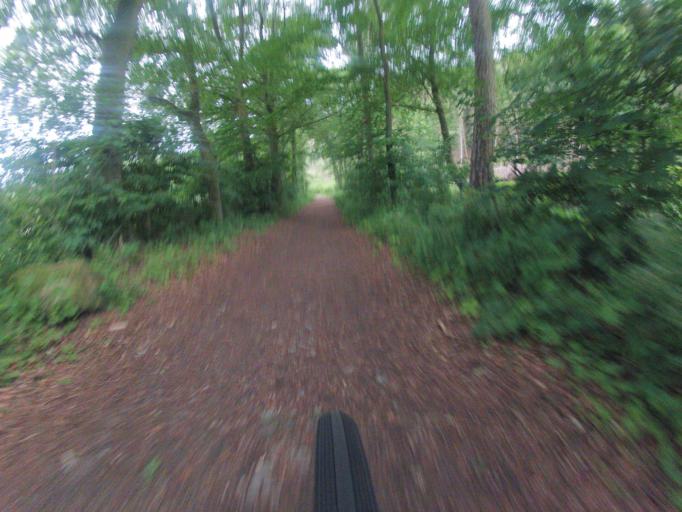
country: DE
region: North Rhine-Westphalia
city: Ibbenburen
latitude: 52.2351
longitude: 7.7409
